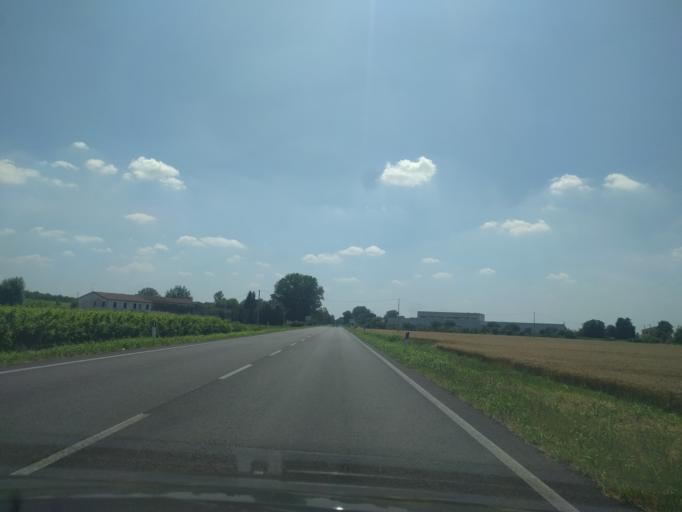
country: IT
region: Emilia-Romagna
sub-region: Provincia di Ferrara
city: Francolino
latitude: 44.9098
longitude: 11.6517
